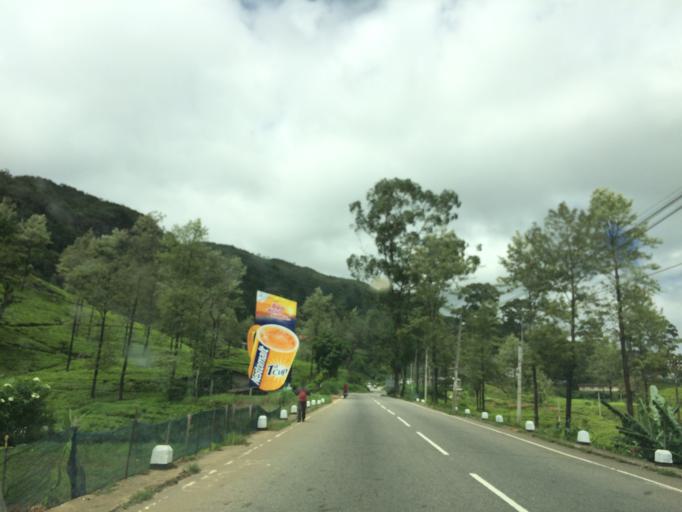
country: LK
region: Central
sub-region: Nuwara Eliya District
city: Nuwara Eliya
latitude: 7.0209
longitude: 80.7236
